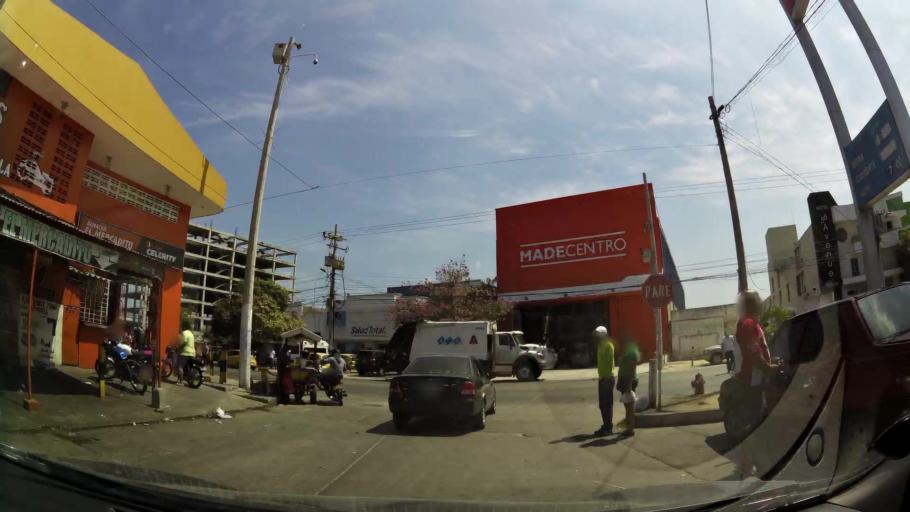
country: CO
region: Atlantico
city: Barranquilla
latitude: 10.9558
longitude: -74.8066
